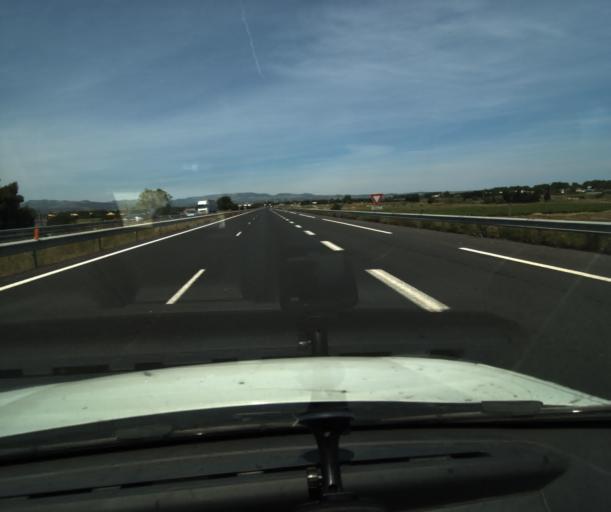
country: FR
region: Languedoc-Roussillon
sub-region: Departement des Pyrenees-Orientales
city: Rivesaltes
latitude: 42.7566
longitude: 2.8923
